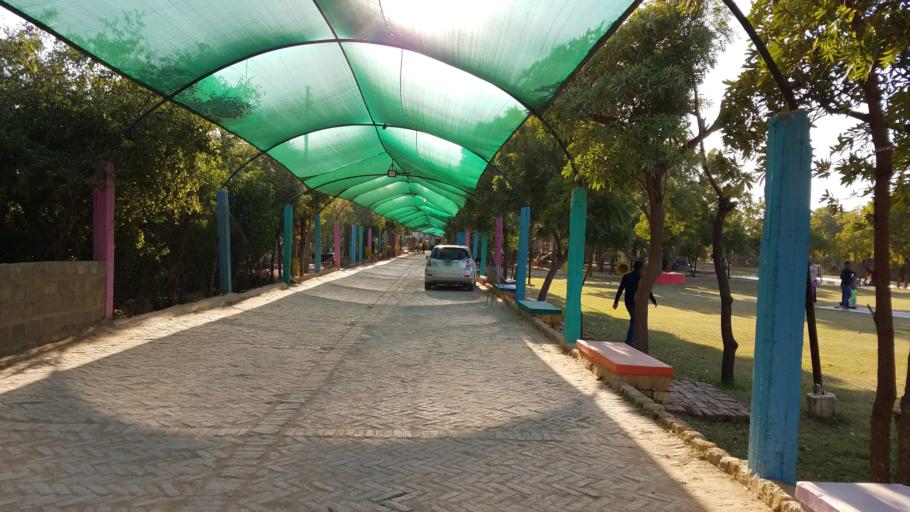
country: PK
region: Sindh
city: Malir Cantonment
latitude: 24.9414
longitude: 67.2644
